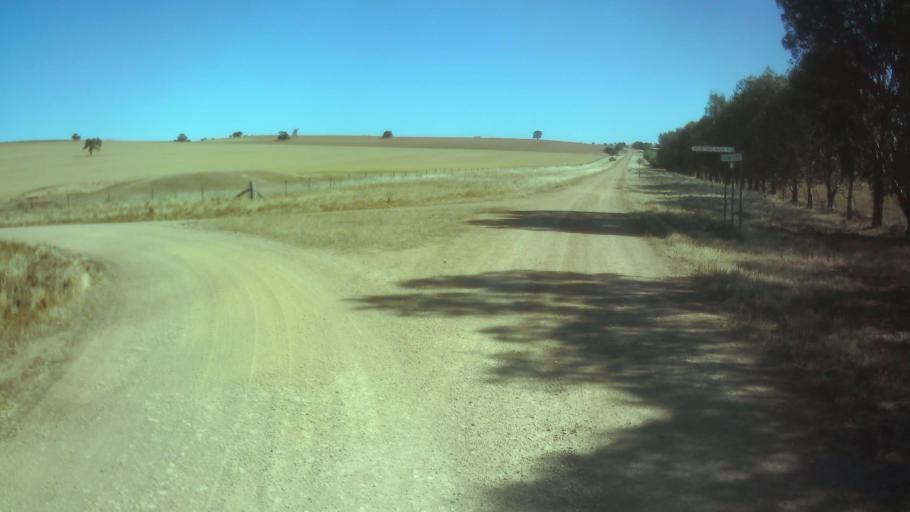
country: AU
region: New South Wales
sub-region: Weddin
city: Grenfell
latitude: -33.9943
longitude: 148.3568
